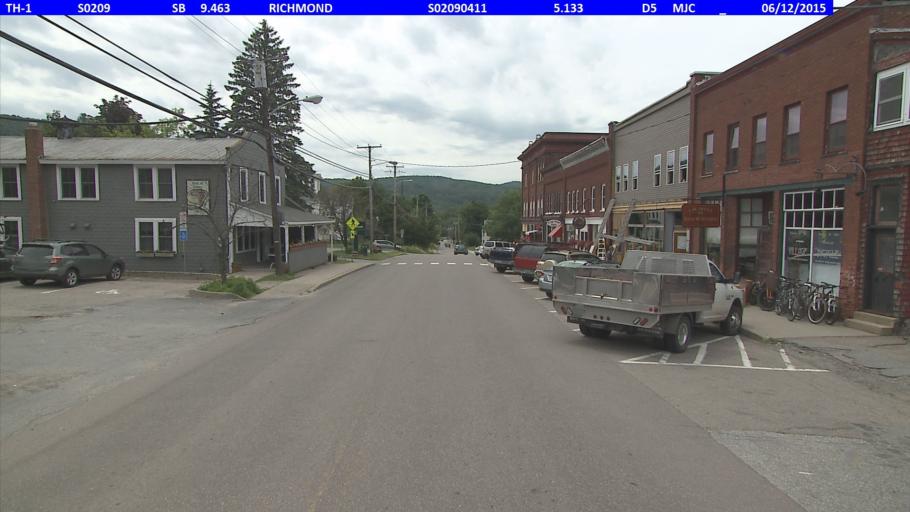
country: US
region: Vermont
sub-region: Chittenden County
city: Williston
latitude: 44.4051
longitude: -72.9931
